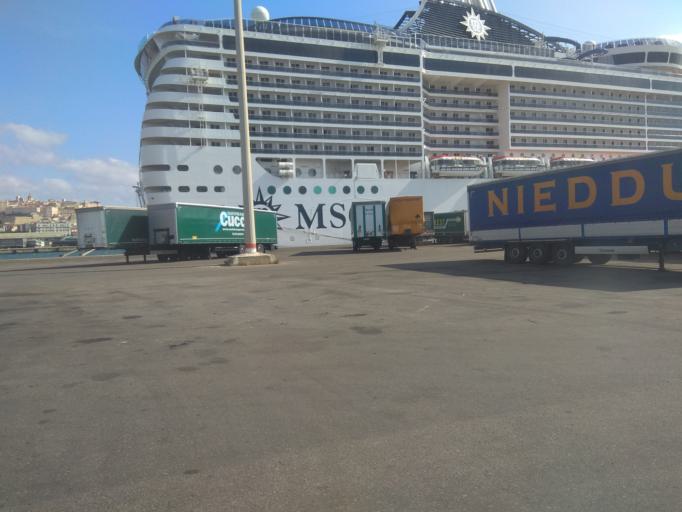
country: IT
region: Sardinia
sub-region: Provincia di Cagliari
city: Cagliari
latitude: 39.2102
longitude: 9.1038
